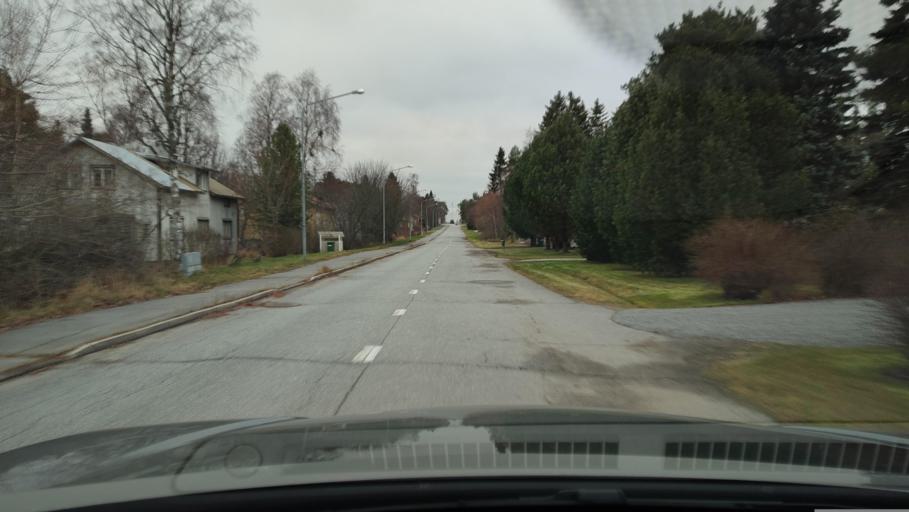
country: FI
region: Ostrobothnia
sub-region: Sydosterbotten
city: Kristinestad
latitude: 62.2673
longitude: 21.3935
